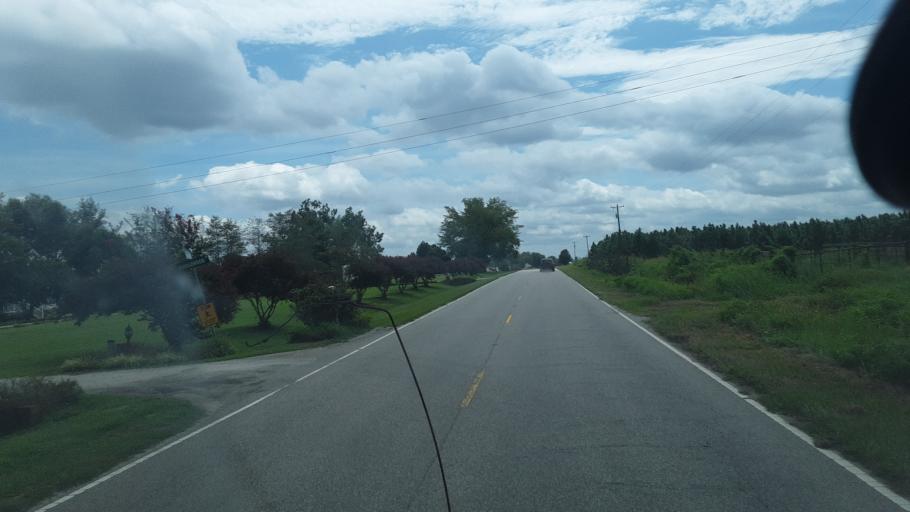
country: US
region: North Carolina
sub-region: Robeson County
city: Fairmont
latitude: 34.3922
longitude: -79.1220
